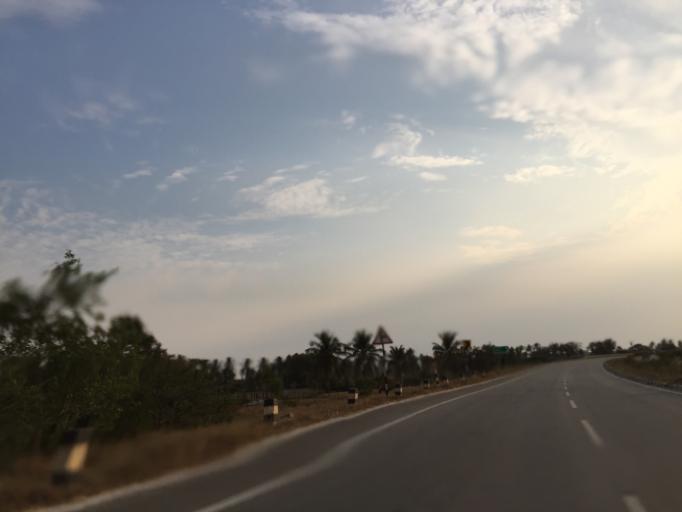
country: IN
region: Karnataka
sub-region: Chikkaballapur
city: Chik Ballapur
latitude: 13.3932
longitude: 77.7404
